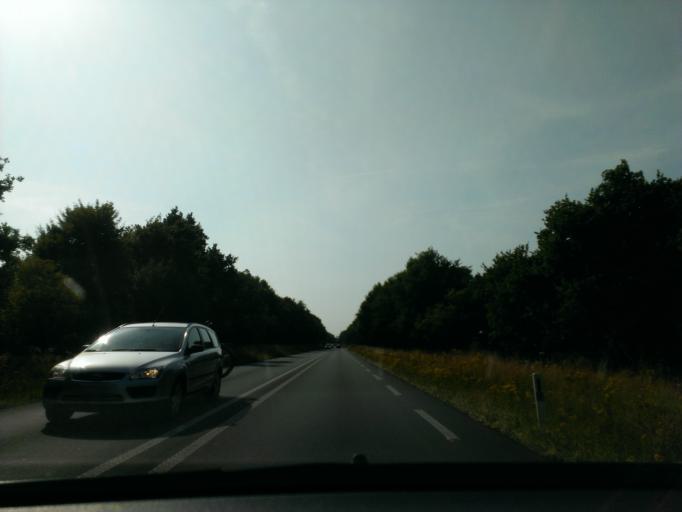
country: NL
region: Gelderland
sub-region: Gemeente Epe
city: Epe
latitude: 52.3349
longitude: 6.0037
